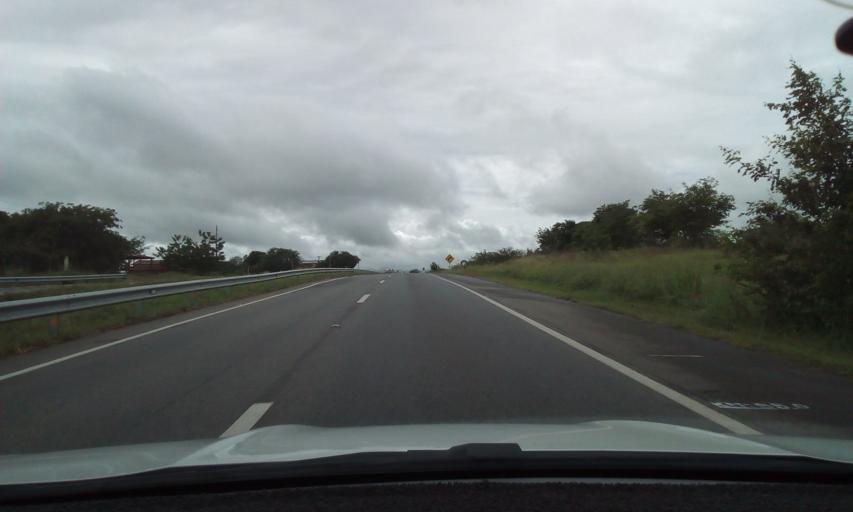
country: BR
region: Paraiba
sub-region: Gurinhem
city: Gurinhem
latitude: -7.1952
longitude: -35.4844
